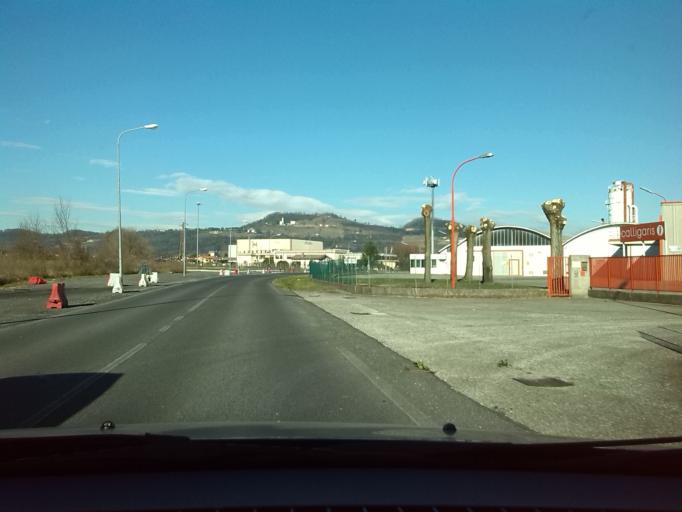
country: IT
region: Friuli Venezia Giulia
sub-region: Provincia di Gorizia
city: Cormons
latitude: 45.9459
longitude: 13.4619
